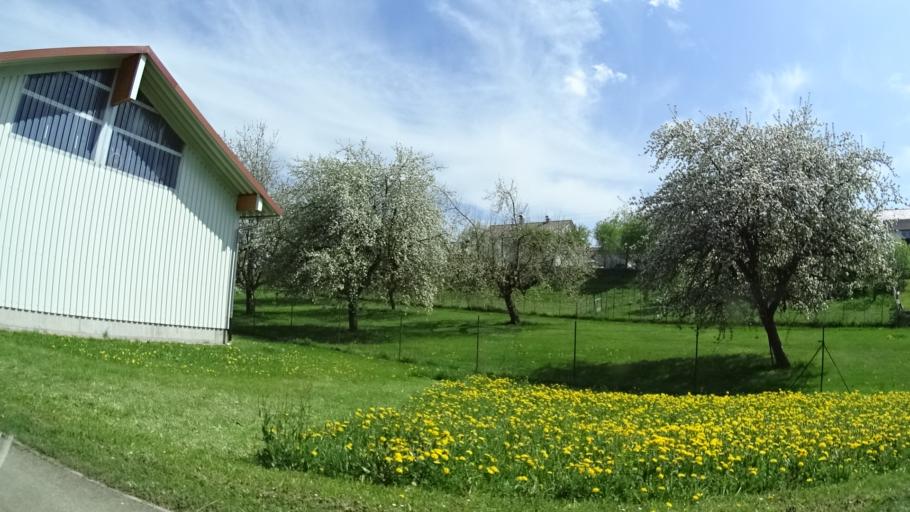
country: DE
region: Baden-Wuerttemberg
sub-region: Freiburg Region
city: Dietingen
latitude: 48.2039
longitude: 8.6431
